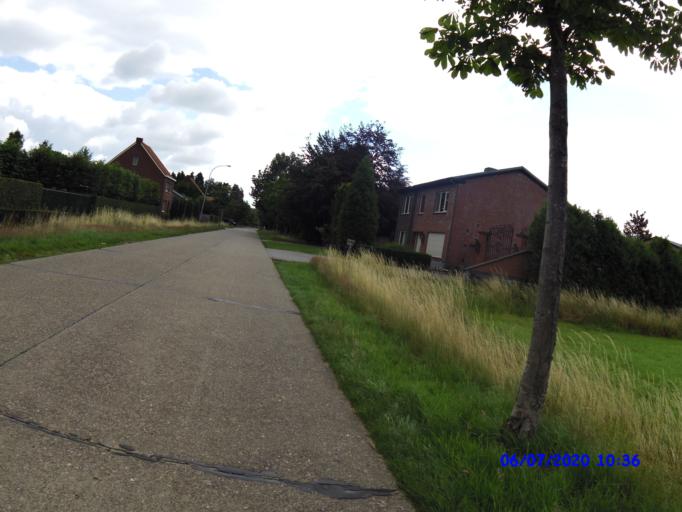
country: BE
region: Flanders
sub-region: Provincie Antwerpen
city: Oud-Turnhout
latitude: 51.3046
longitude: 4.9987
